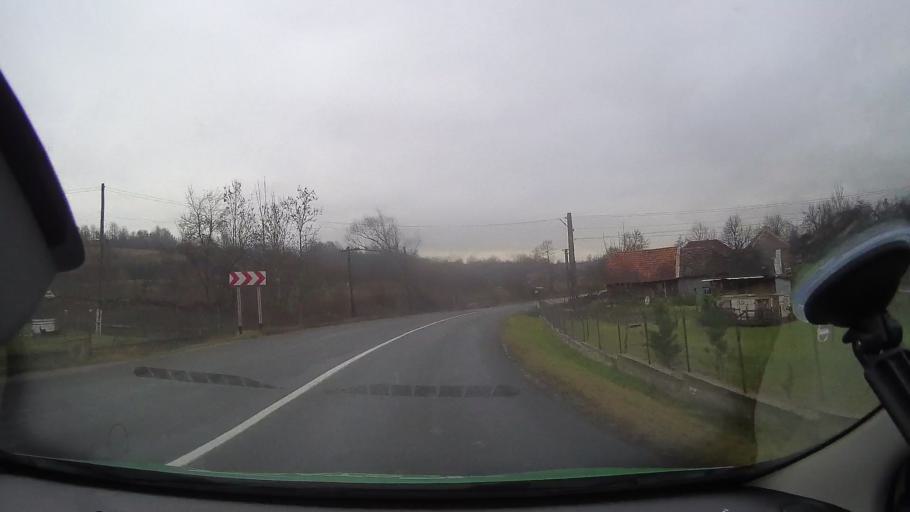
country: RO
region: Arad
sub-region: Comuna Varfurile
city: Varfurile
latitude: 46.3219
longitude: 22.5038
